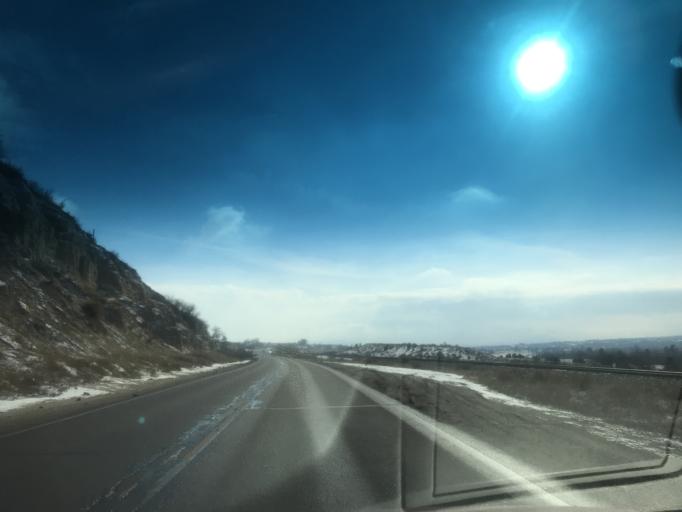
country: US
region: Colorado
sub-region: Douglas County
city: Castle Pines
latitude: 39.4569
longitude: -104.9823
